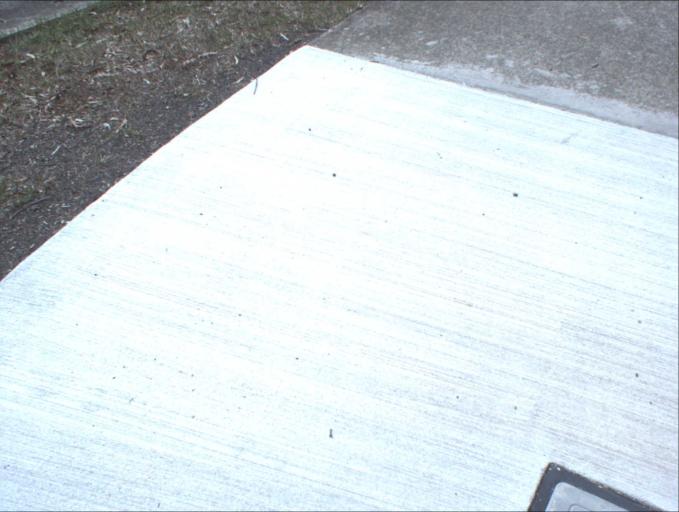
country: AU
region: Queensland
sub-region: Logan
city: Slacks Creek
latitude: -27.6578
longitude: 153.1663
